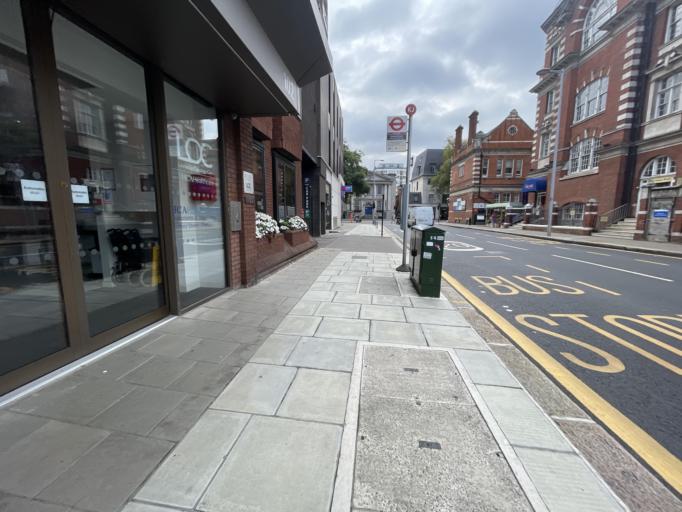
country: GB
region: England
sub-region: Greater London
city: Chelsea
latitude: 51.4880
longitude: -0.1690
